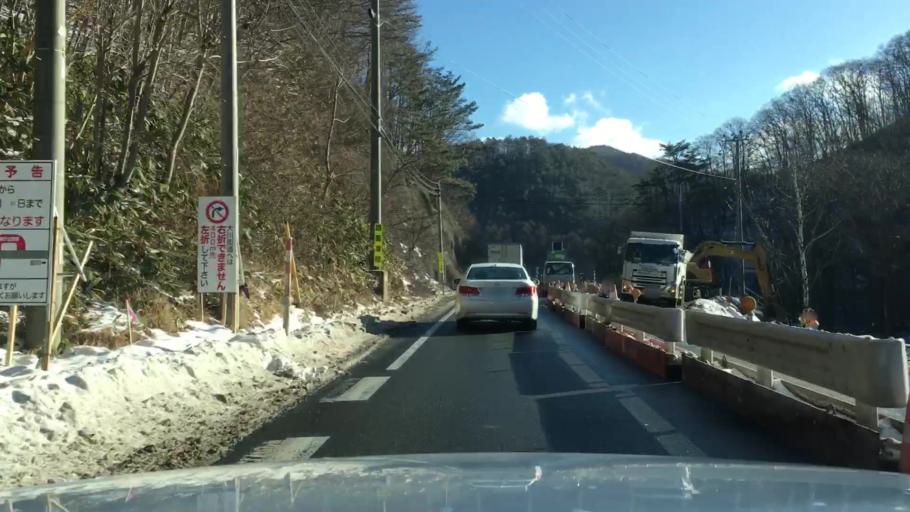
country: JP
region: Iwate
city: Morioka-shi
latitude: 39.6343
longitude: 141.4475
